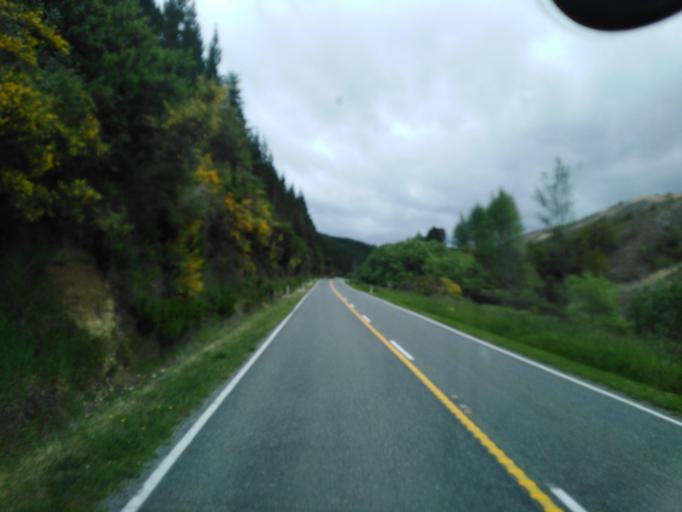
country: NZ
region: Tasman
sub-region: Tasman District
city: Wakefield
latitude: -41.6233
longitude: 172.7430
